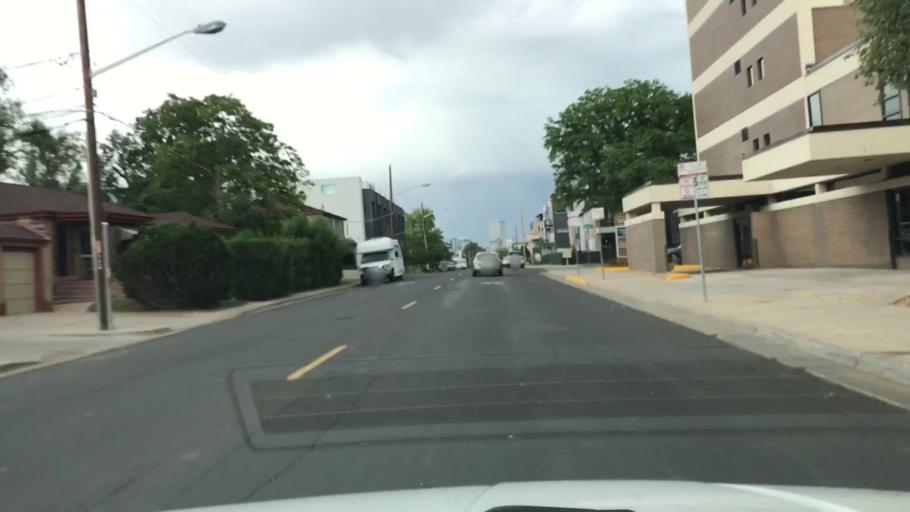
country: US
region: Colorado
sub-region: Jefferson County
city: Edgewater
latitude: 39.7439
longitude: -105.0356
